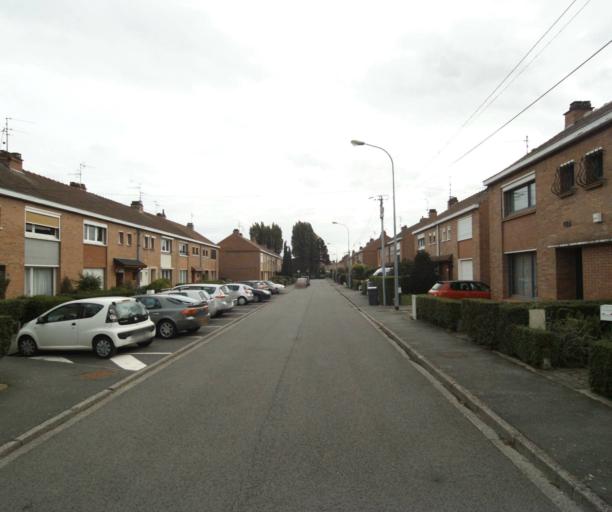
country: FR
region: Nord-Pas-de-Calais
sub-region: Departement du Nord
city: Lambersart
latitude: 50.6504
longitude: 3.0140
